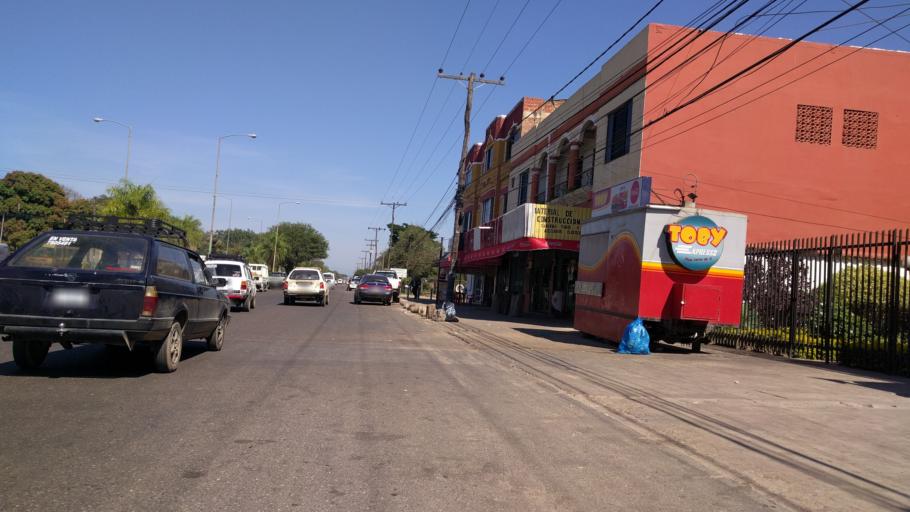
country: BO
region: Santa Cruz
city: Santa Cruz de la Sierra
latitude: -17.8297
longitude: -63.2286
